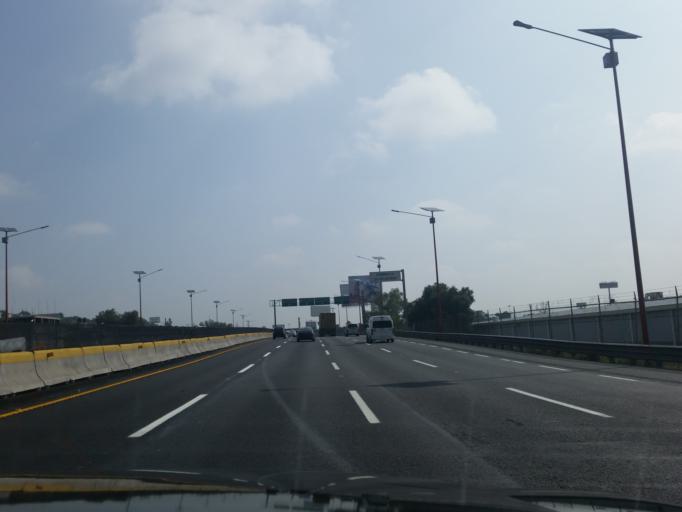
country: MX
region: Mexico
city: Ecatepec
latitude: 19.5806
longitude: -99.0446
